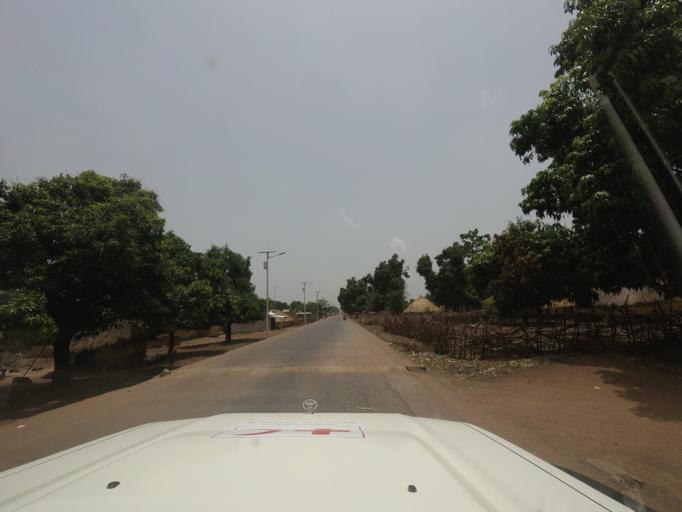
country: GN
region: Faranah
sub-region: Faranah Prefecture
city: Faranah
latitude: 9.7338
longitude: -10.6348
